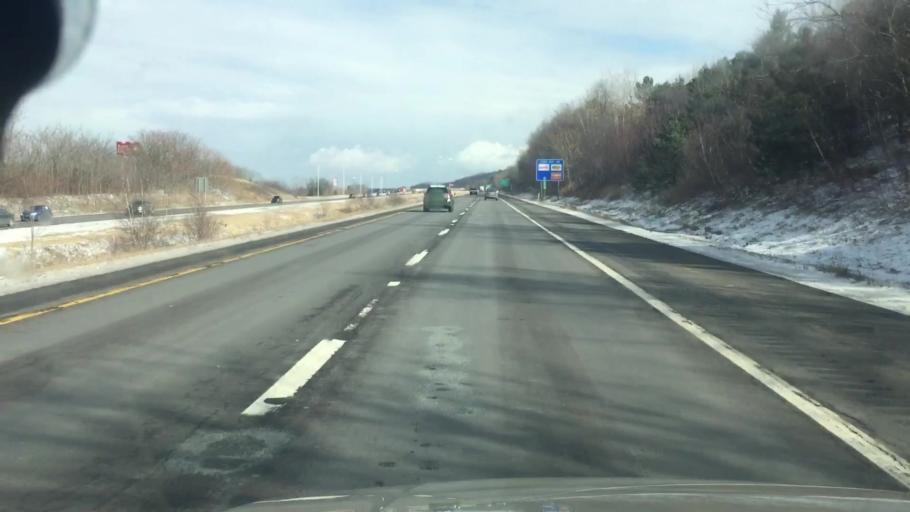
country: US
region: Pennsylvania
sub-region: Luzerne County
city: Georgetown
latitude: 41.2308
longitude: -75.8609
